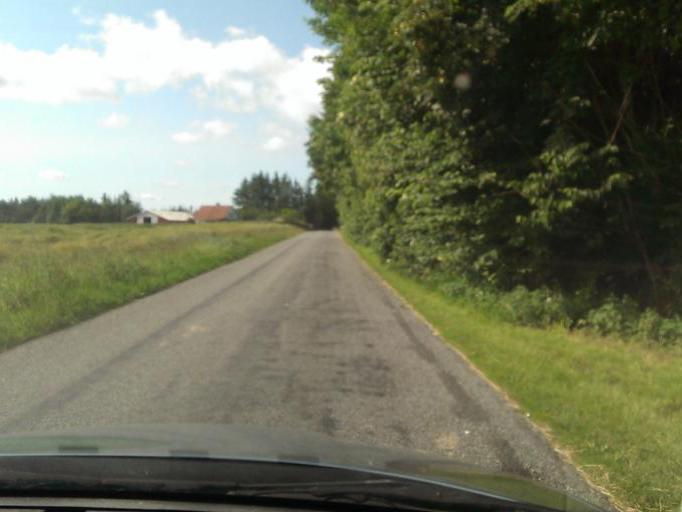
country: DK
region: North Denmark
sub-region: Alborg Kommune
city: Vestbjerg
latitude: 57.1939
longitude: 9.9273
